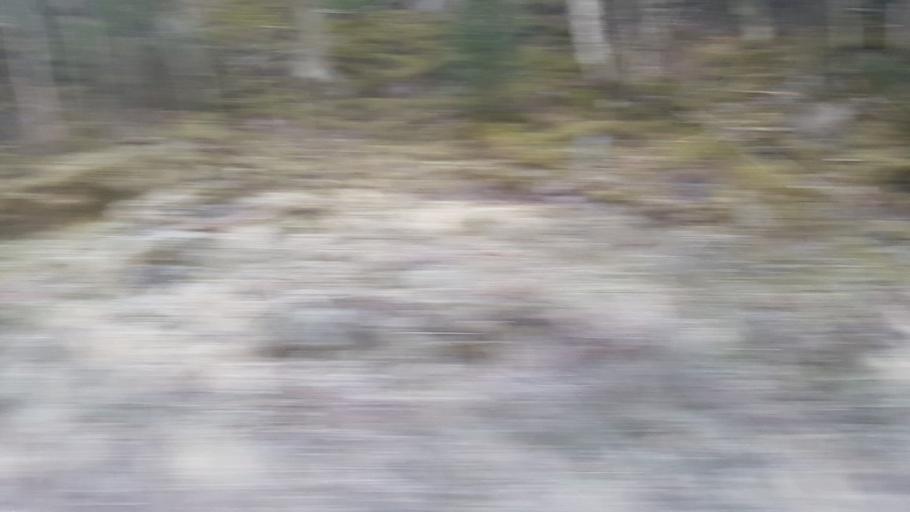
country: NO
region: Nord-Trondelag
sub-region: Stjordal
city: Stjordalshalsen
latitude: 63.5874
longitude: 11.0092
